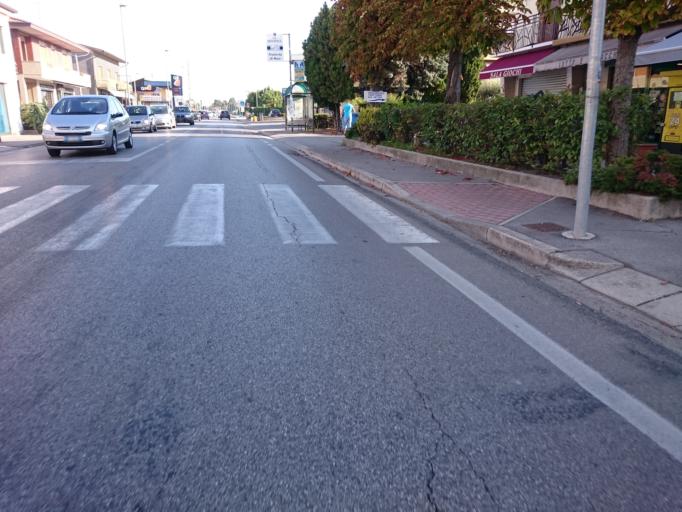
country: IT
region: Veneto
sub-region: Provincia di Padova
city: Masera di Padova
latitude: 45.3240
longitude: 11.8640
